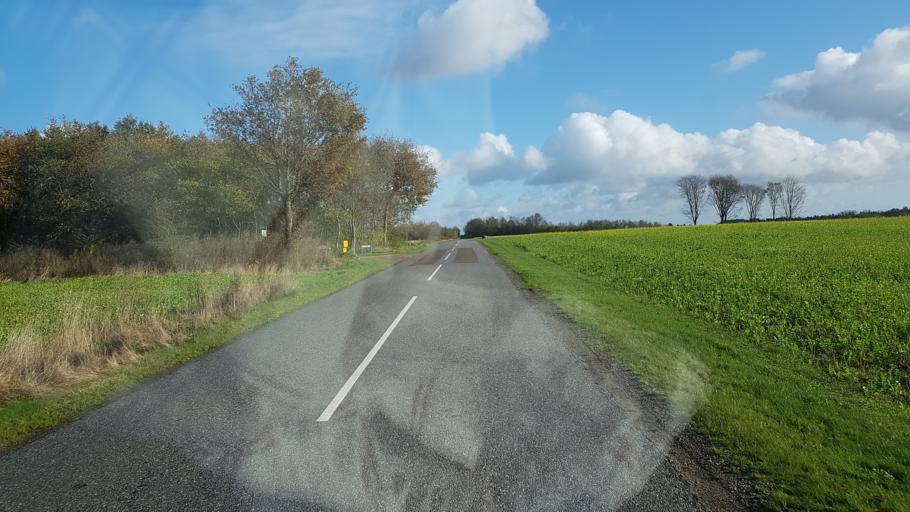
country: DK
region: South Denmark
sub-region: Varde Kommune
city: Olgod
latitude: 55.6949
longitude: 8.7063
